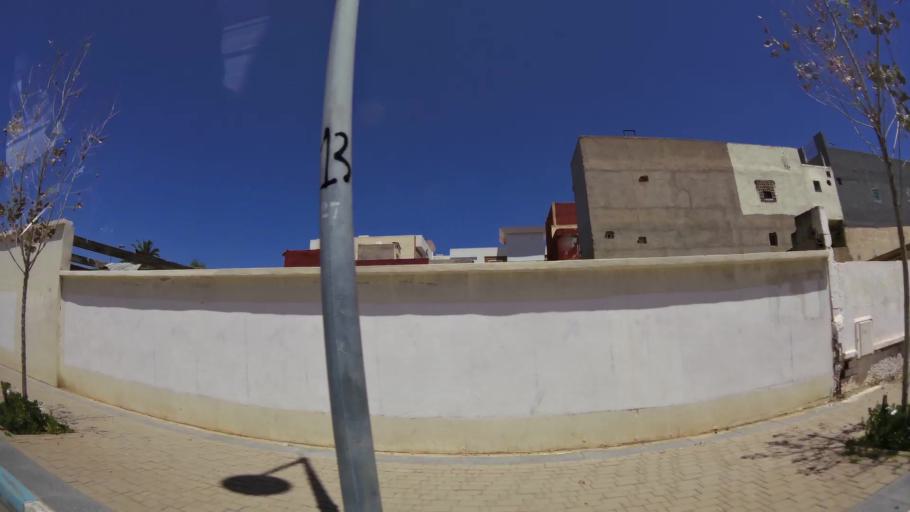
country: MA
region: Oriental
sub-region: Berkane-Taourirt
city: Madagh
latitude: 35.0835
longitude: -2.2226
